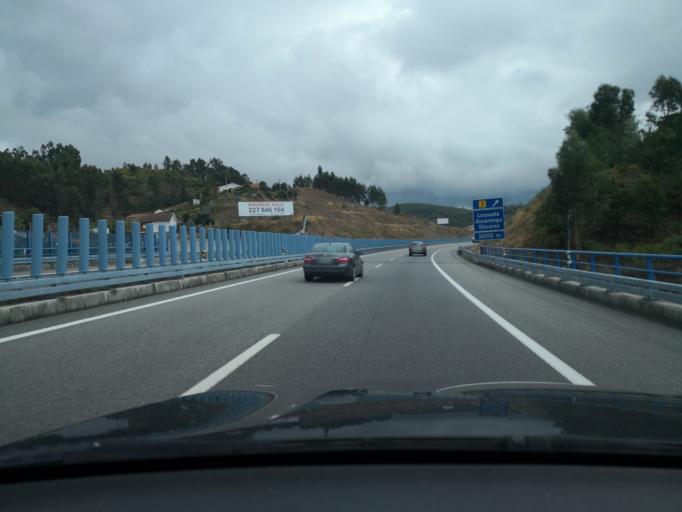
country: PT
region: Porto
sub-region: Lousada
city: Lousada
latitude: 41.2961
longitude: -8.3051
